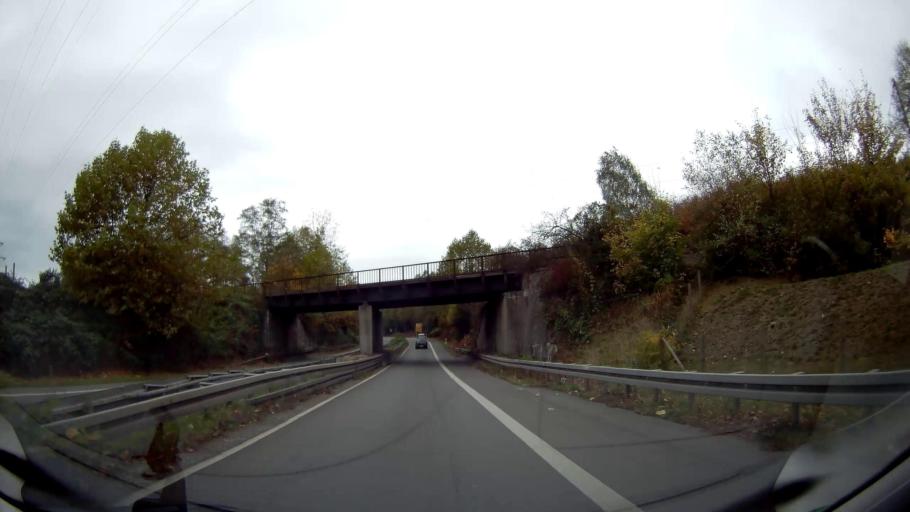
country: DE
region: North Rhine-Westphalia
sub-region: Regierungsbezirk Munster
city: Gladbeck
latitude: 51.5214
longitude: 6.9880
